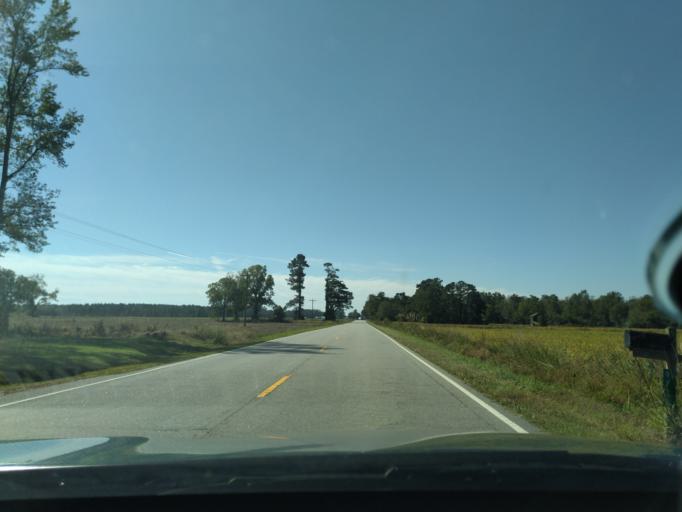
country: US
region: North Carolina
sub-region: Washington County
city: Plymouth
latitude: 35.7262
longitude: -76.7493
